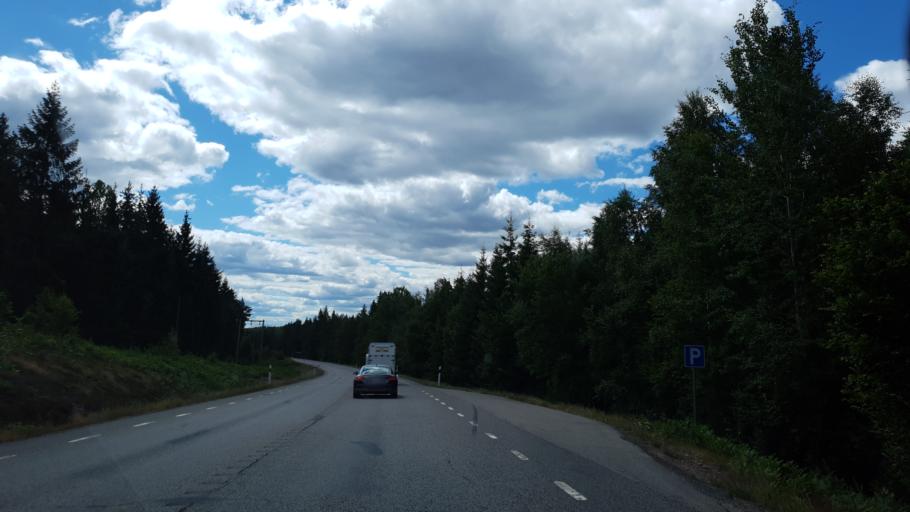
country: SE
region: Kronoberg
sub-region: Vaxjo Kommun
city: Braas
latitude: 57.1542
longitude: 15.1589
